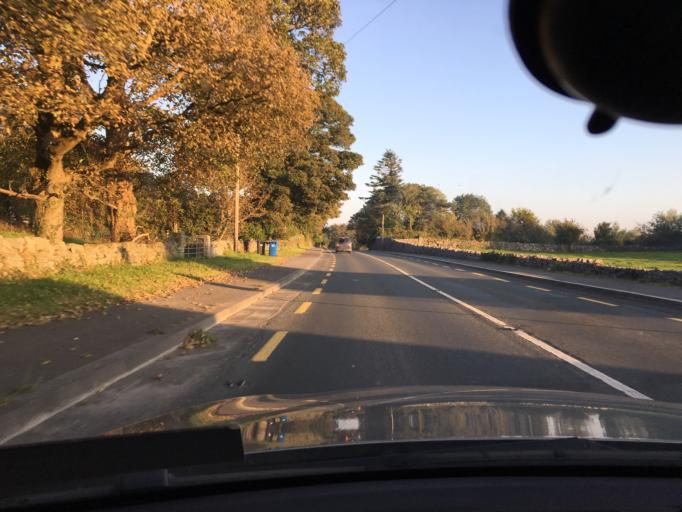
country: IE
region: Connaught
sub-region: County Galway
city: Oughterard
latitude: 53.3943
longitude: -9.2528
